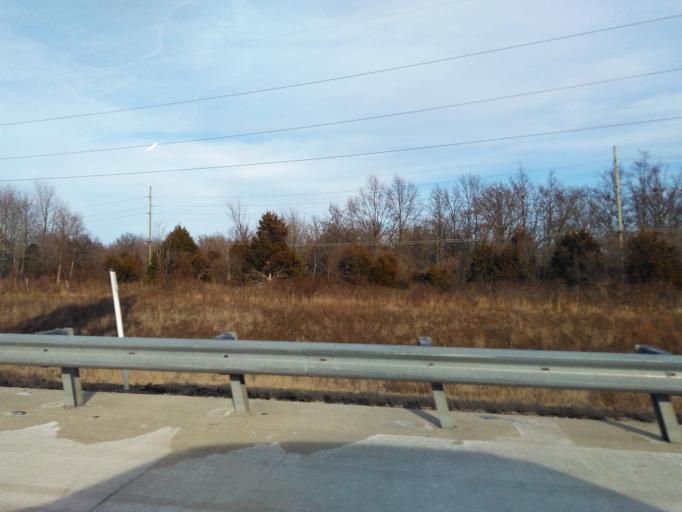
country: US
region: Illinois
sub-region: Jefferson County
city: Mount Vernon
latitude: 38.2942
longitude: -88.9438
